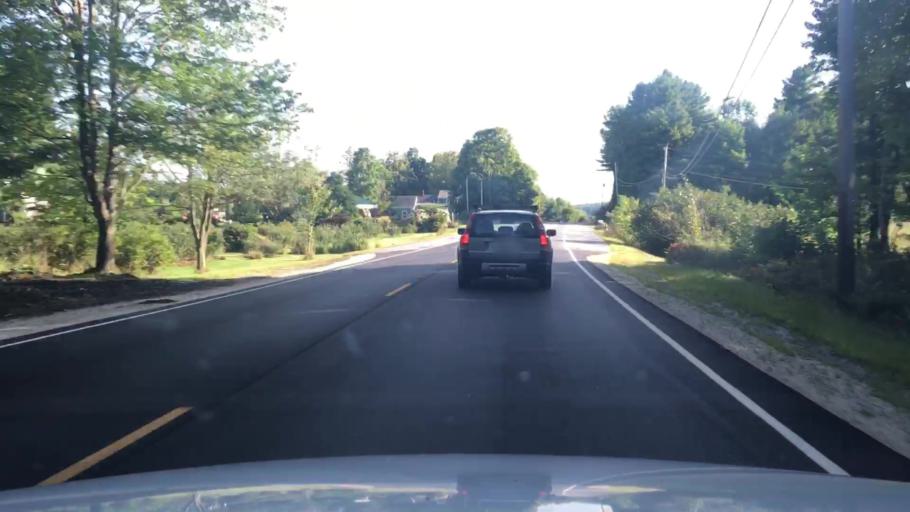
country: US
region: Maine
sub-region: Cumberland County
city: Cumberland Center
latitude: 43.7662
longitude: -70.3008
